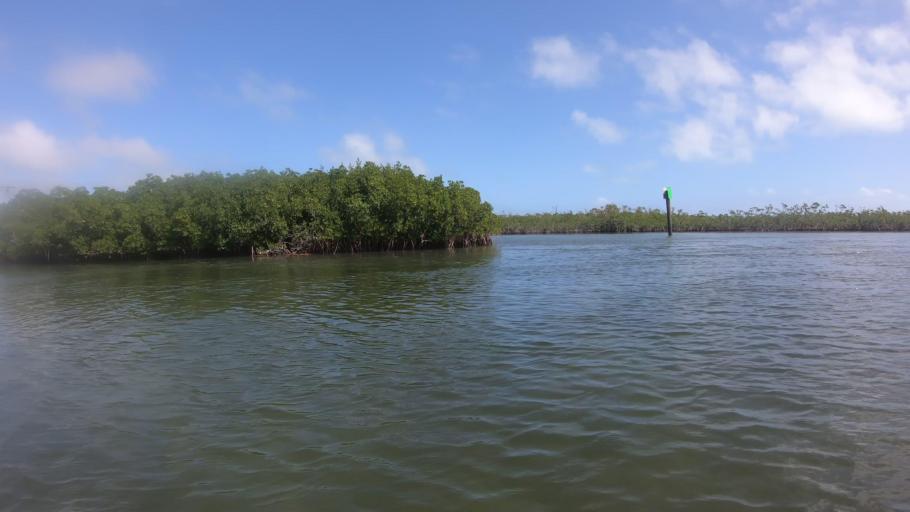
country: US
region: Florida
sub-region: Monroe County
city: Key Largo
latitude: 25.1214
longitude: -80.4031
